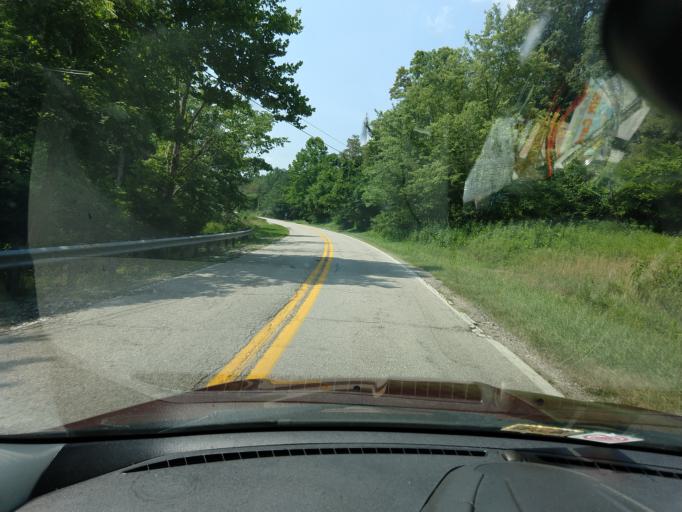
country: US
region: West Virginia
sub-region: Mason County
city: New Haven
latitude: 38.9041
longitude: -81.9371
